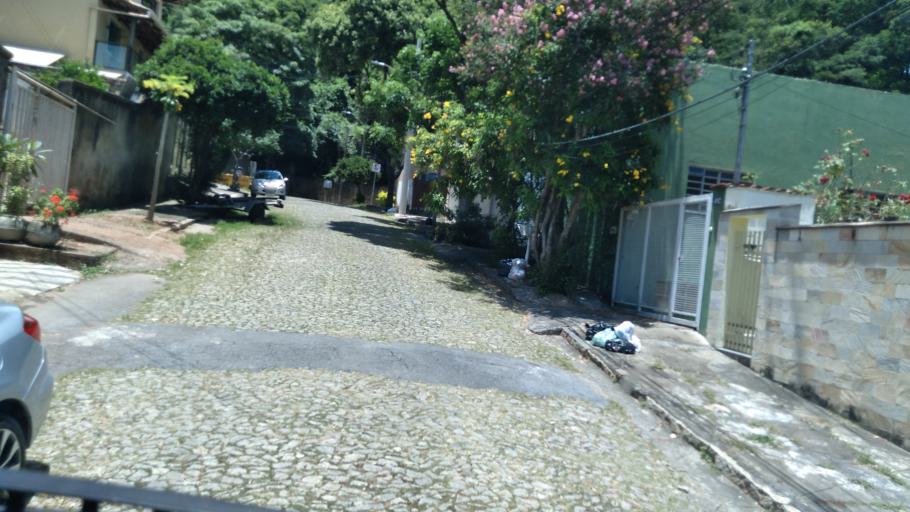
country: BR
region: Minas Gerais
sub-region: Belo Horizonte
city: Belo Horizonte
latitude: -19.9173
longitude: -43.9918
